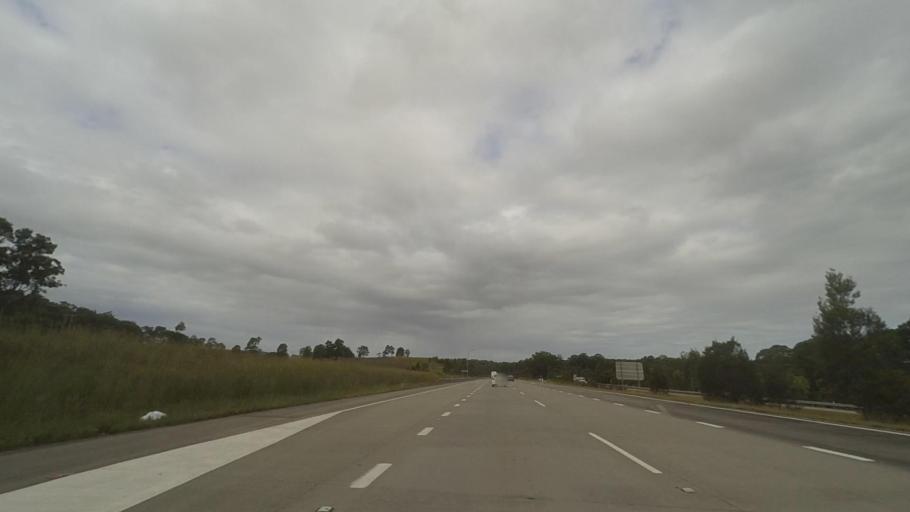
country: AU
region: New South Wales
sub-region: Port Stephens Shire
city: Port Stephens
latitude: -32.6377
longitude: 152.0321
